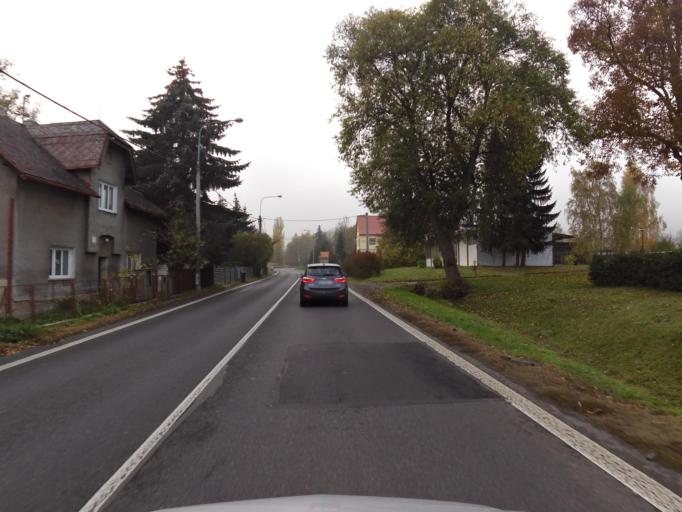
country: CZ
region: Ustecky
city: Libouchec
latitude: 50.7606
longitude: 14.0590
